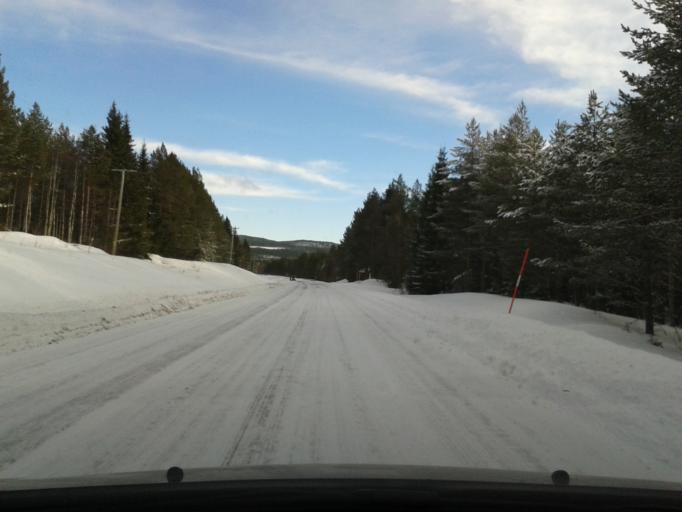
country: SE
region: Vaesterbotten
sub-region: Asele Kommun
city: Asele
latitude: 64.3421
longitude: 17.0153
